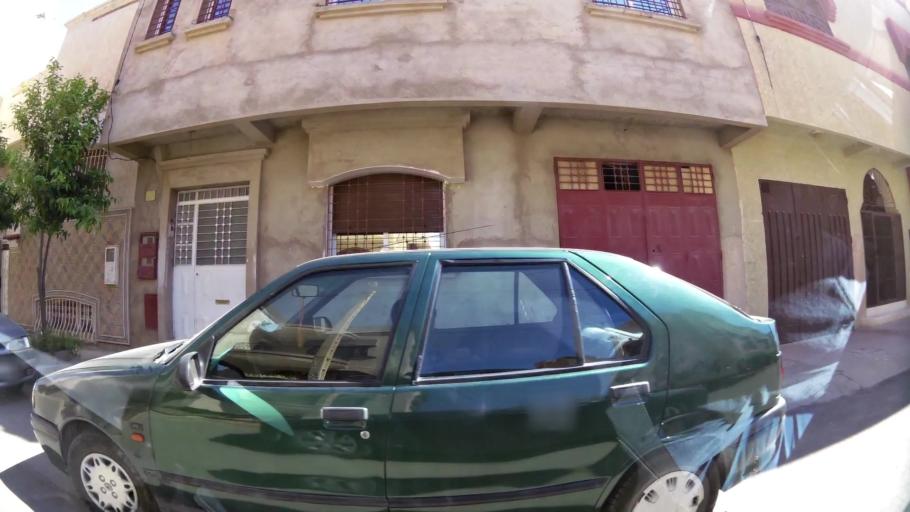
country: MA
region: Oriental
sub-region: Oujda-Angad
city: Oujda
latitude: 34.6554
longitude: -1.9154
